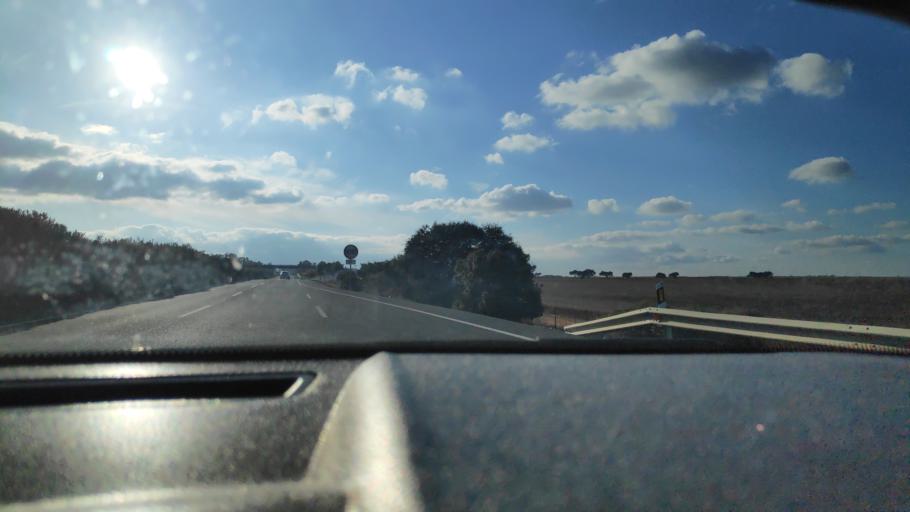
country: ES
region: Andalusia
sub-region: Provincia de Sevilla
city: La Luisiana
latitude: 37.5247
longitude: -5.3054
